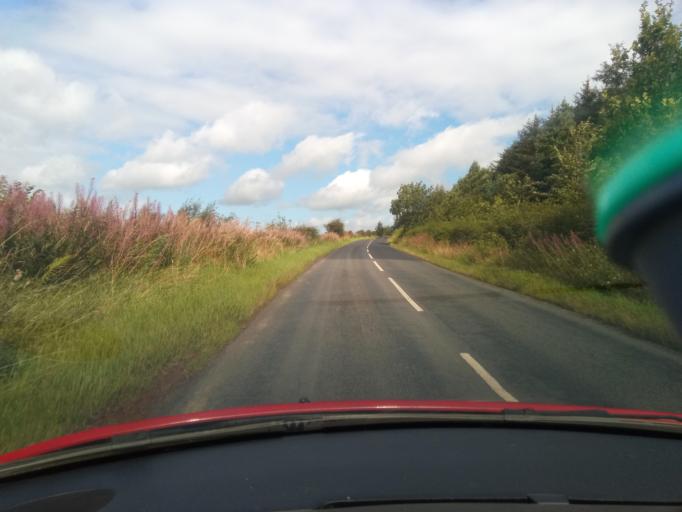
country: GB
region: Scotland
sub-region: The Scottish Borders
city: Melrose
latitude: 55.5717
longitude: -2.7318
